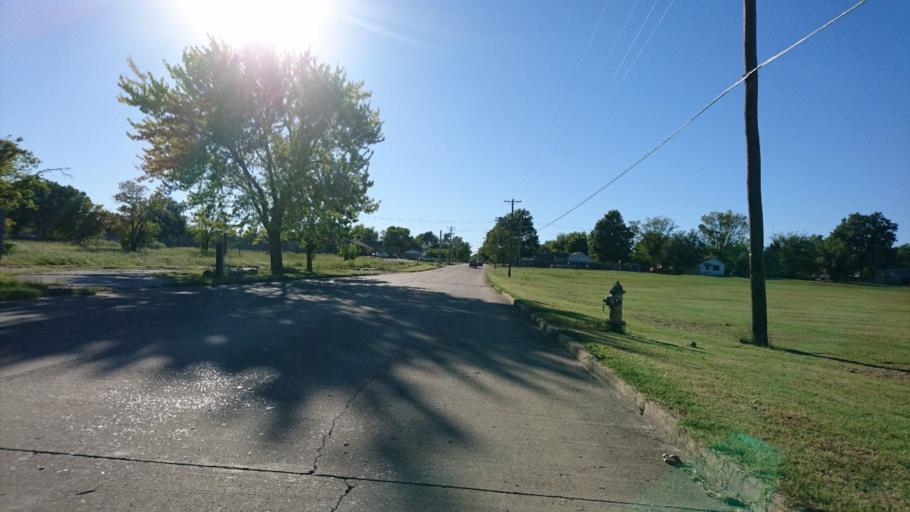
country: US
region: Oklahoma
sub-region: Rogers County
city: Claremore
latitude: 36.3110
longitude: -95.6221
